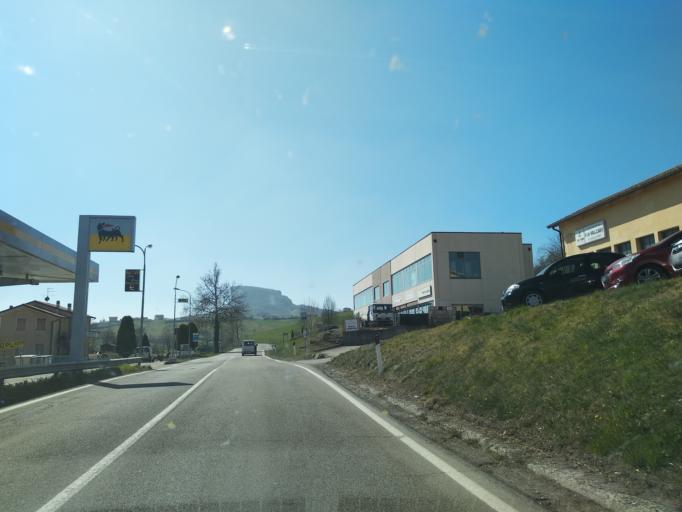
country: IT
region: Emilia-Romagna
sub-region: Provincia di Reggio Emilia
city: Felina
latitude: 44.4445
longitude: 10.4458
